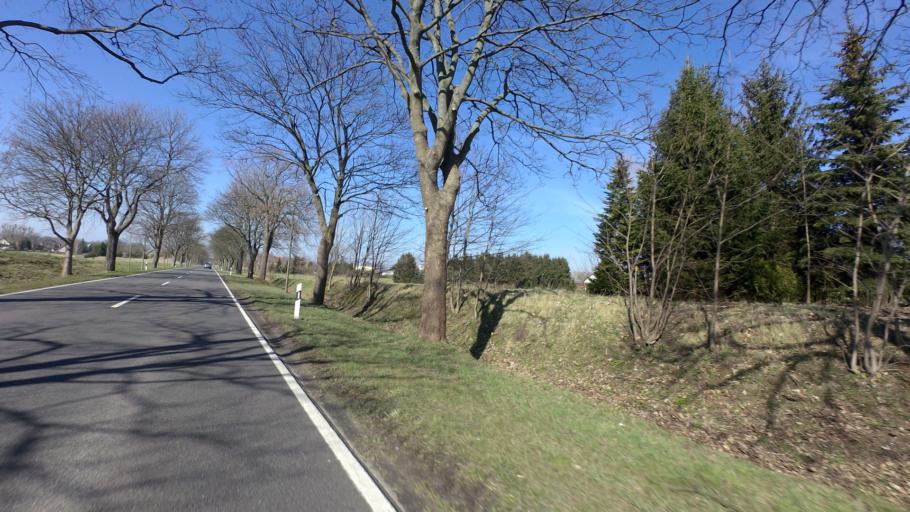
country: DE
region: Brandenburg
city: Eberswalde
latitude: 52.7690
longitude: 13.8387
